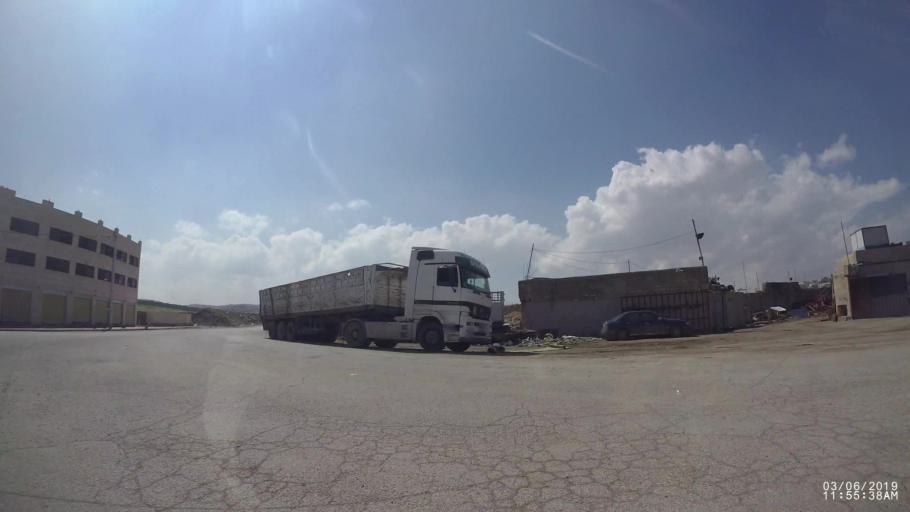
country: JO
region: Zarqa
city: Russeifa
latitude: 31.9847
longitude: 36.0107
